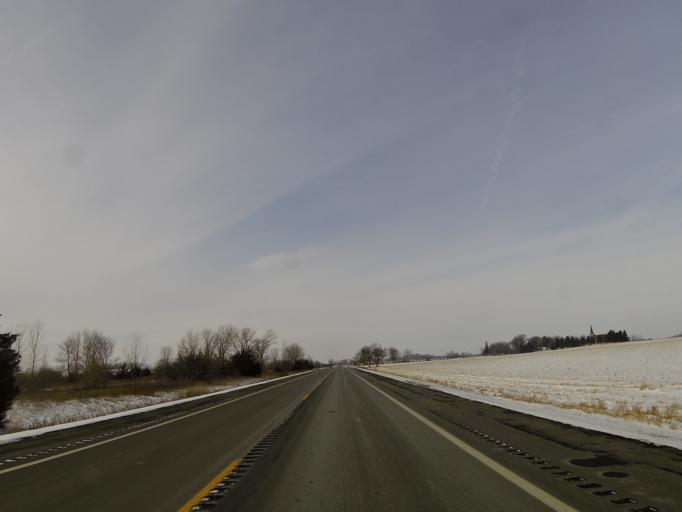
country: US
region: Minnesota
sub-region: McLeod County
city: Hutchinson
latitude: 44.9149
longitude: -94.4568
